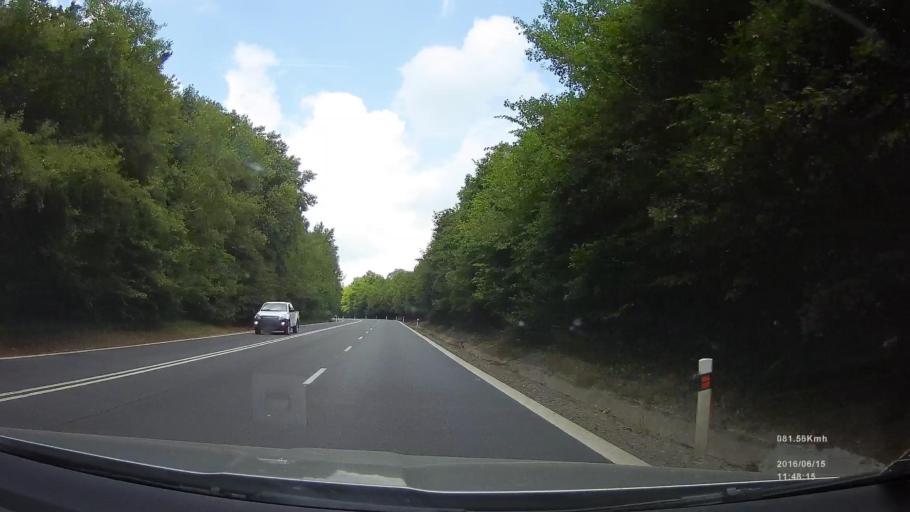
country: SK
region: Kosicky
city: Kosice
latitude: 48.7314
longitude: 21.3224
